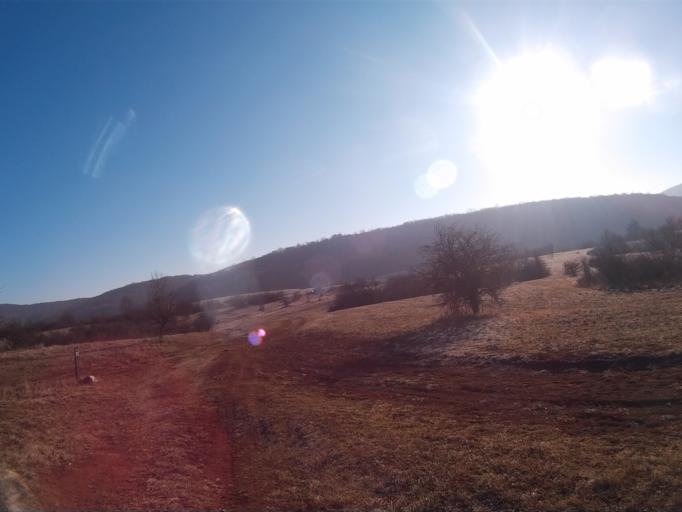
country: HU
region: Borsod-Abauj-Zemplen
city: Rudabanya
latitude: 48.4929
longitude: 20.5542
